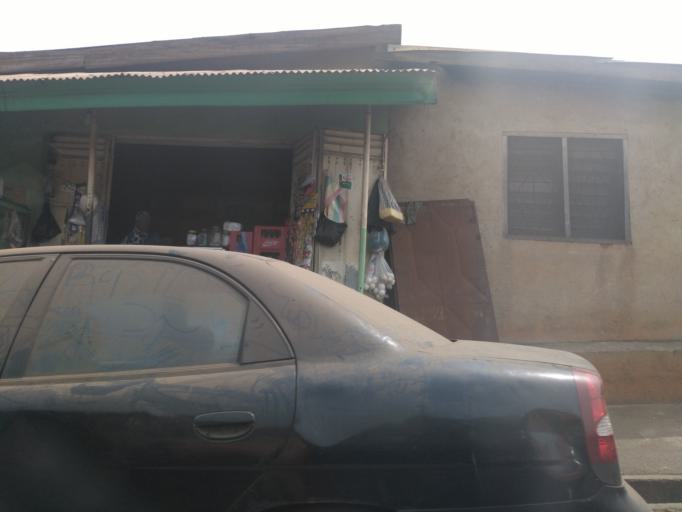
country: GH
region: Ashanti
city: Kumasi
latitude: 6.7048
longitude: -1.6091
